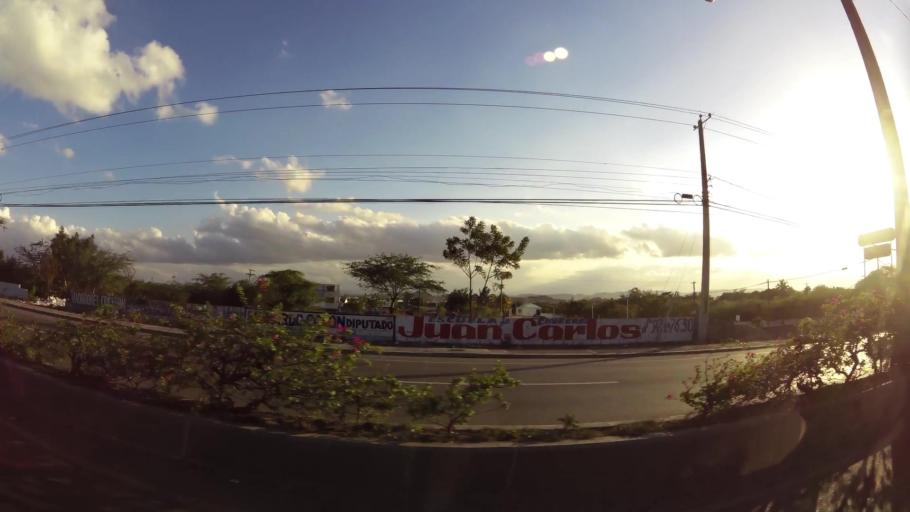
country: DO
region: Santiago
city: Palmar Arriba
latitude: 19.4939
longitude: -70.7305
